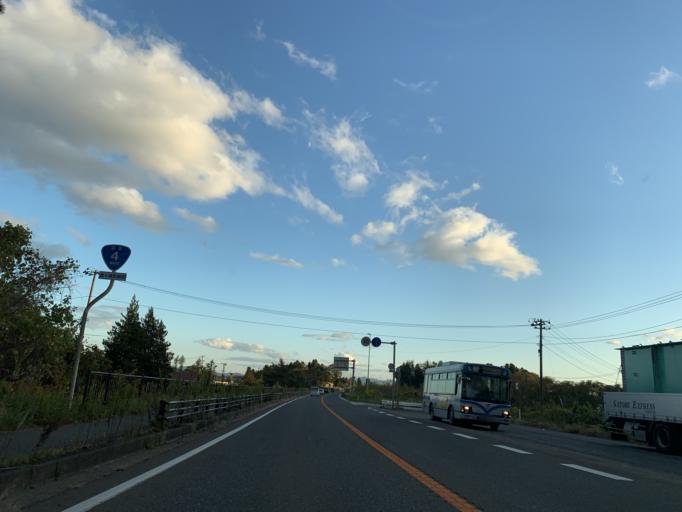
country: JP
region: Iwate
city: Kitakami
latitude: 39.2077
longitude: 141.1077
